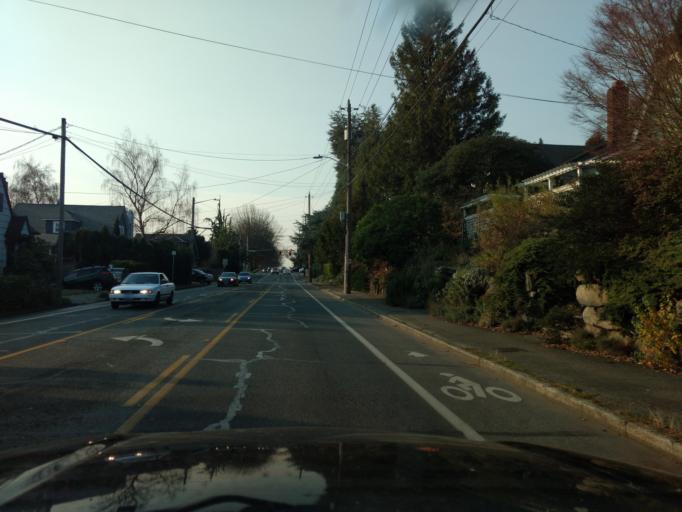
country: US
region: Washington
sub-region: King County
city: Shoreline
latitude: 47.6831
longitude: -122.3101
